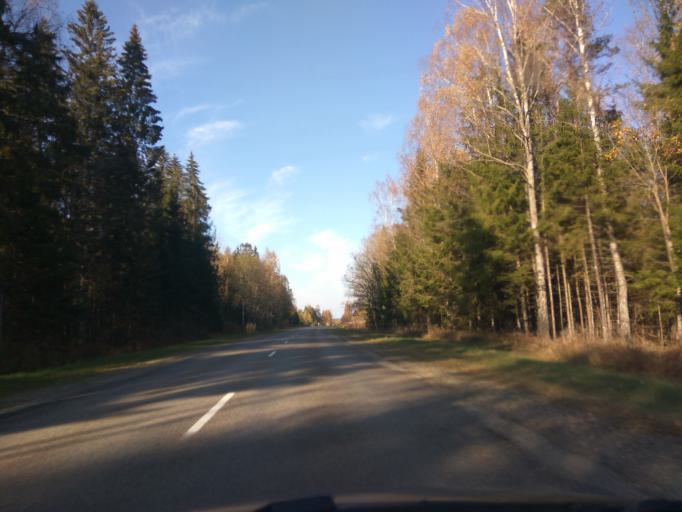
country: LV
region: Kuldigas Rajons
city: Kuldiga
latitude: 57.0471
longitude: 21.8234
